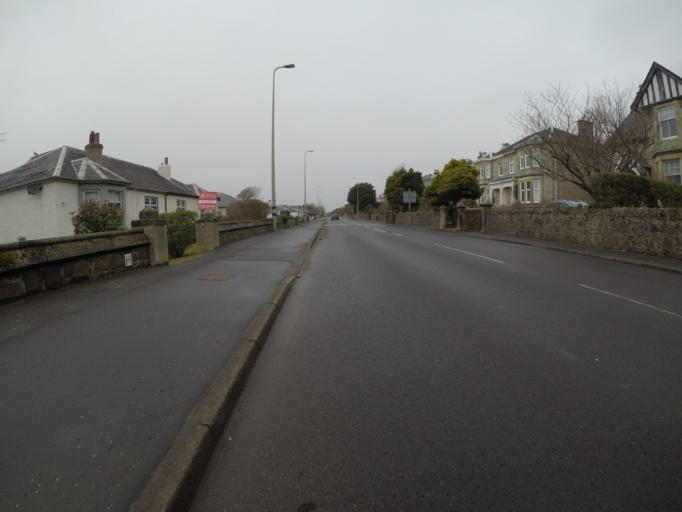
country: GB
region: Scotland
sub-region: North Ayrshire
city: West Kilbride
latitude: 55.6903
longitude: -4.8648
